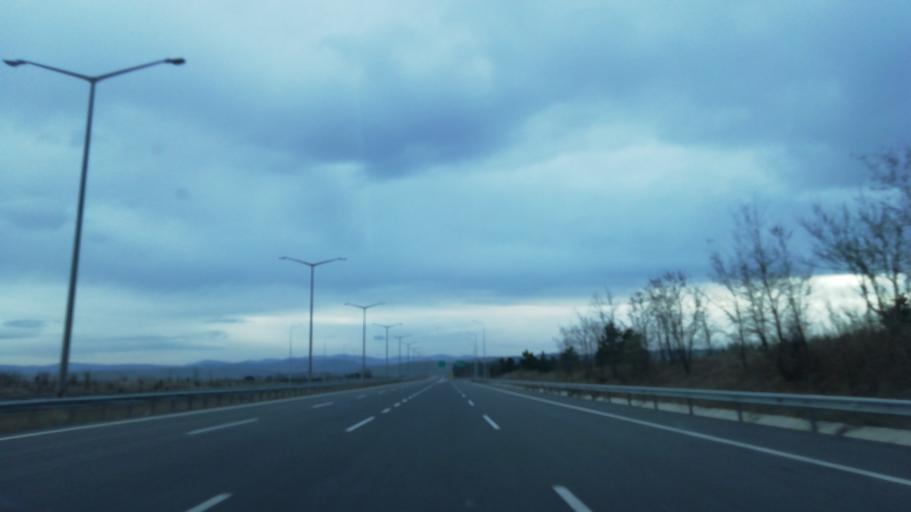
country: TR
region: Bolu
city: Gerede
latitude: 40.7448
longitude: 32.1968
